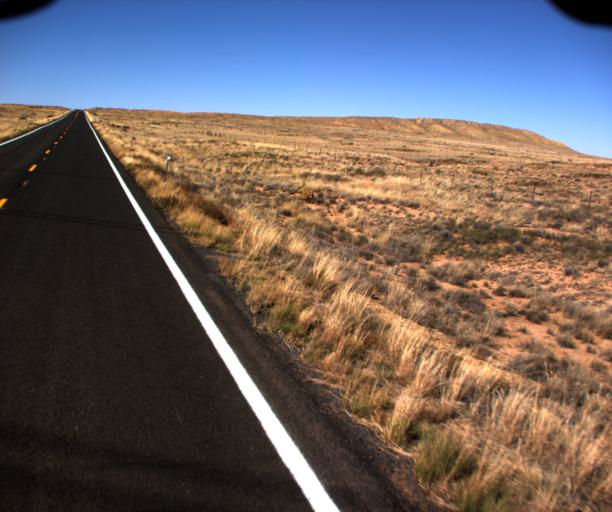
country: US
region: Arizona
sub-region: Coconino County
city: Tuba City
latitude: 35.9523
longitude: -110.9247
